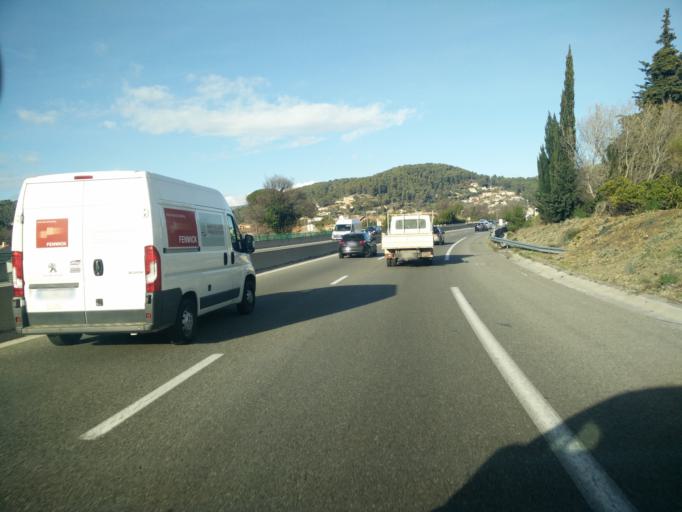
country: FR
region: Provence-Alpes-Cote d'Azur
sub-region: Departement du Var
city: Sollies-Pont
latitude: 43.1899
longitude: 6.0370
